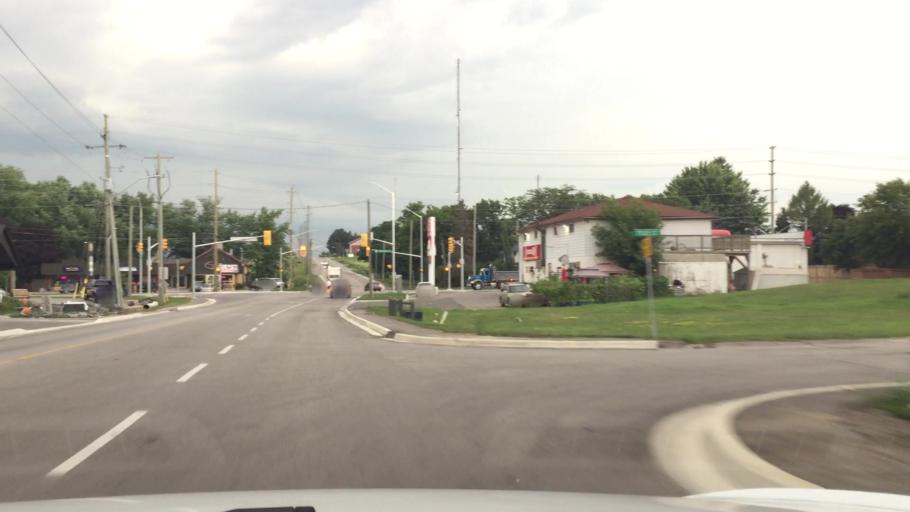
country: CA
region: Ontario
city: Oshawa
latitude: 43.9487
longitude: -78.8051
